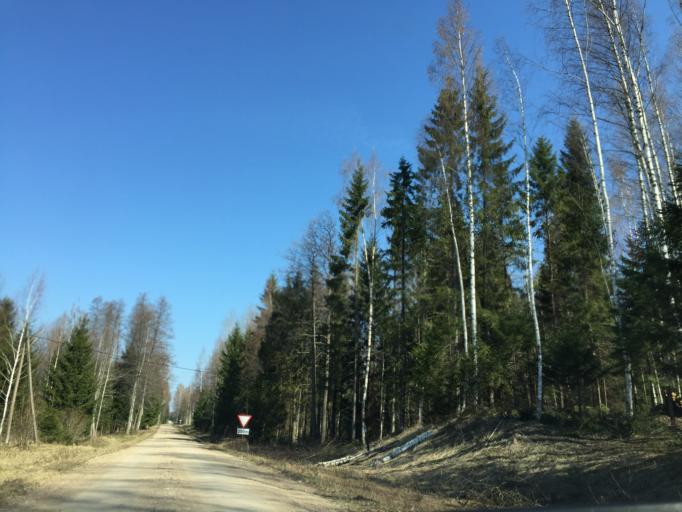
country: EE
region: Tartu
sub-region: Alatskivi vald
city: Kallaste
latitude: 58.5742
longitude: 26.9449
